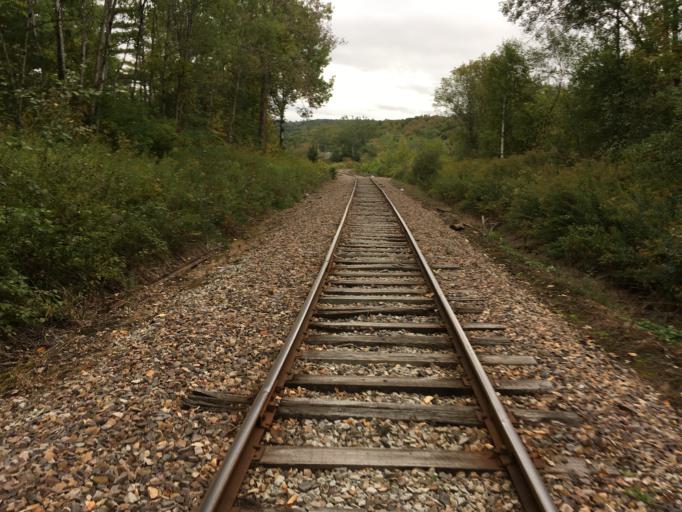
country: US
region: Vermont
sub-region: Washington County
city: Montpelier
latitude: 44.2251
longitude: -72.5498
